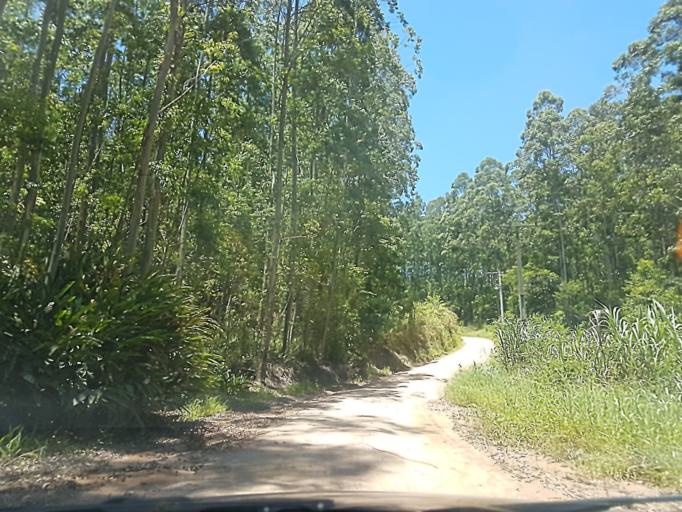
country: BR
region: Santa Catarina
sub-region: Braco Do Norte
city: Braco do Norte
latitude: -28.3918
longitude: -49.1262
